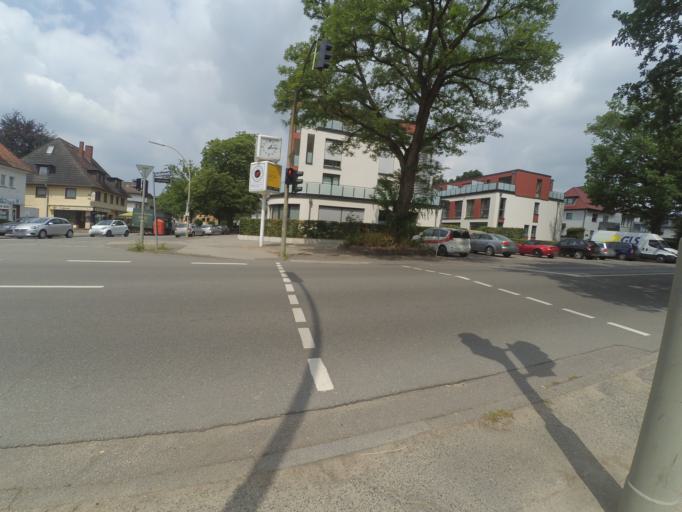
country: DE
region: Hamburg
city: Sasel
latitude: 53.6505
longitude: 10.0979
